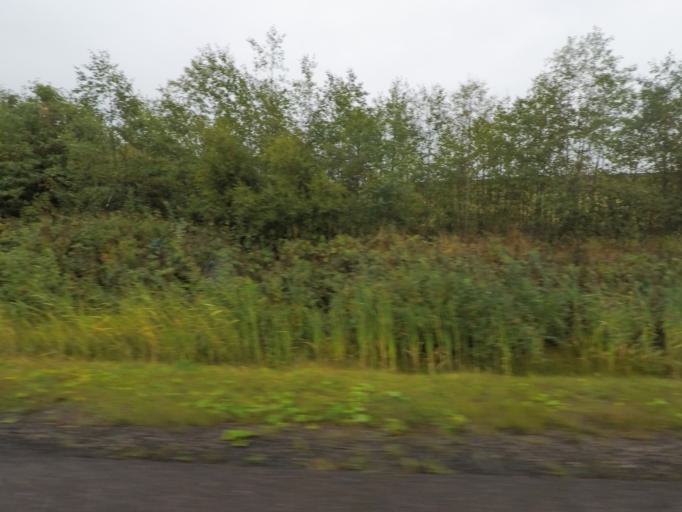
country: FI
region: Northern Savo
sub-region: Varkaus
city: Varkaus
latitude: 62.2791
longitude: 27.8668
